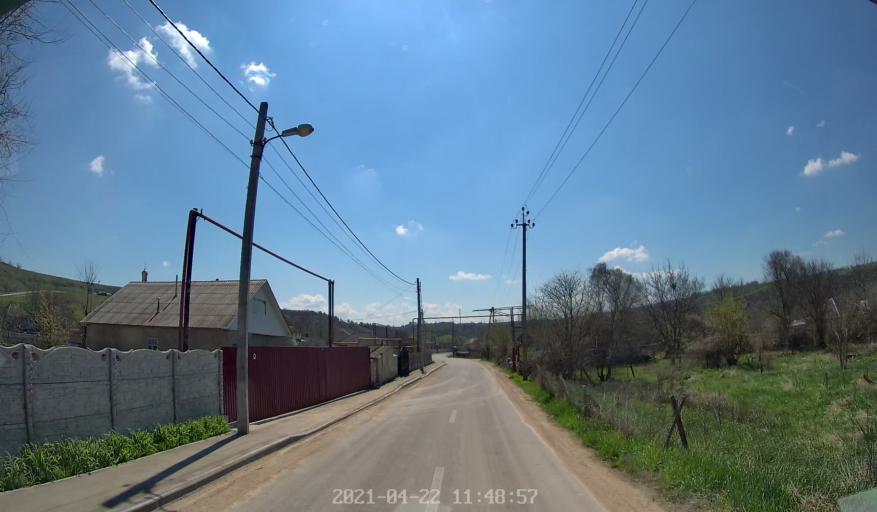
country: MD
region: Chisinau
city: Ciorescu
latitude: 47.1451
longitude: 28.8966
